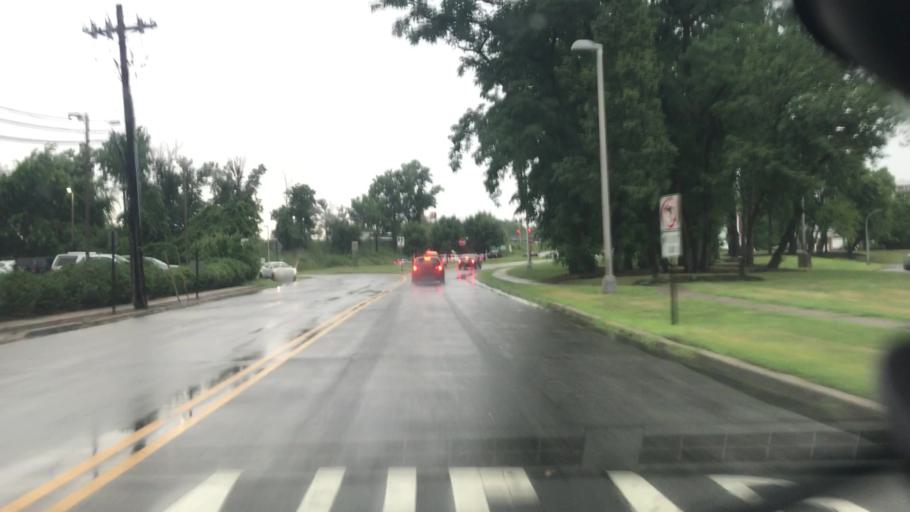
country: US
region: New Jersey
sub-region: Union County
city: Clark
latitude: 40.6253
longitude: -74.3040
